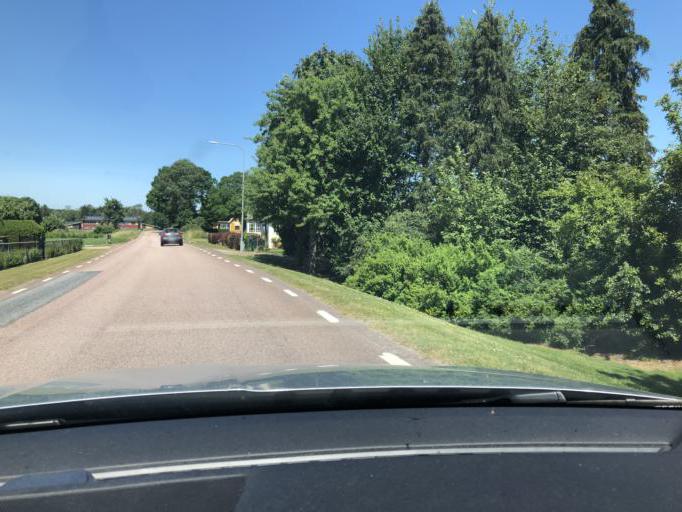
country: SE
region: Blekinge
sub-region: Olofstroms Kommun
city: Jamshog
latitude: 56.1799
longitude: 14.6125
